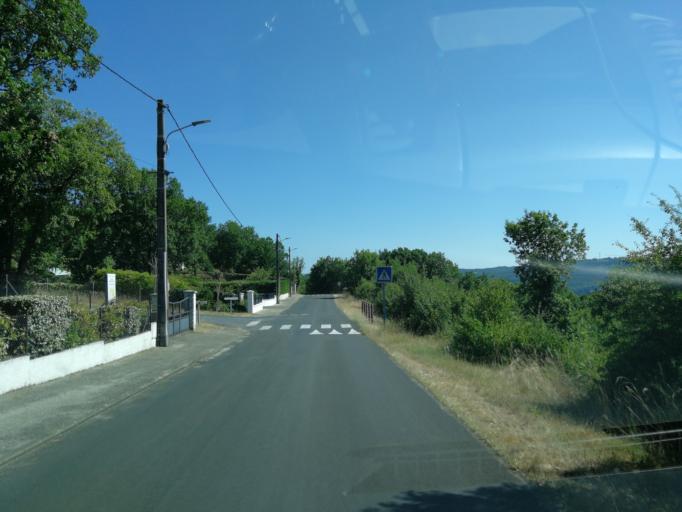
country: FR
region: Midi-Pyrenees
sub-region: Departement du Lot
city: Souillac
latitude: 44.9117
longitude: 1.4821
